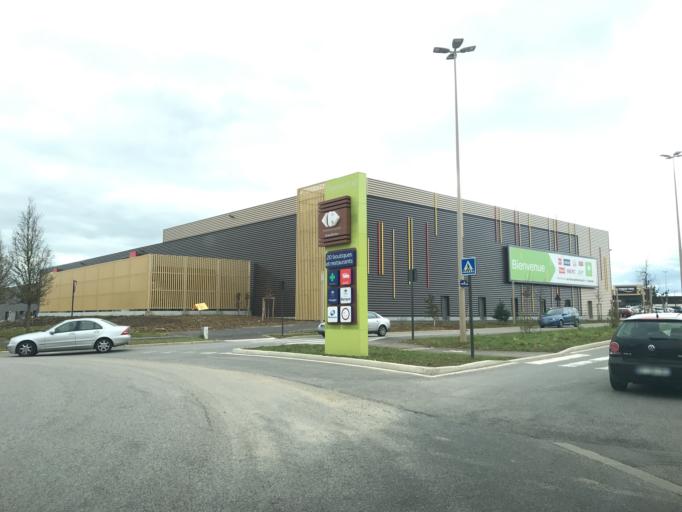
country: FR
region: Haute-Normandie
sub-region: Departement de l'Eure
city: Evreux
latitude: 49.0142
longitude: 1.1789
